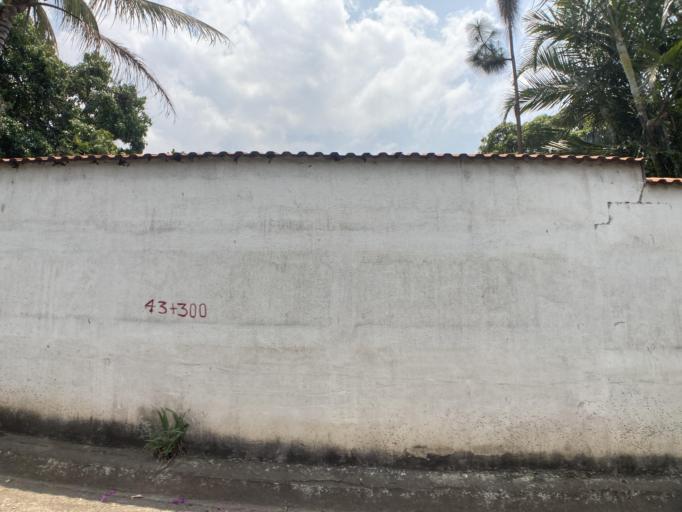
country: GT
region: Guatemala
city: Fraijanes
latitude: 14.3545
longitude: -90.5044
